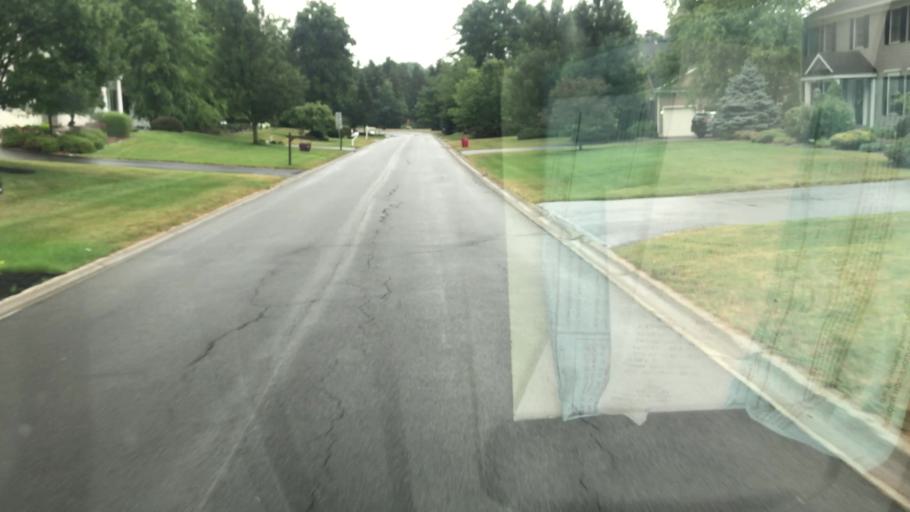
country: US
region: New York
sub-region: Onondaga County
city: Manlius
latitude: 42.9882
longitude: -75.9791
